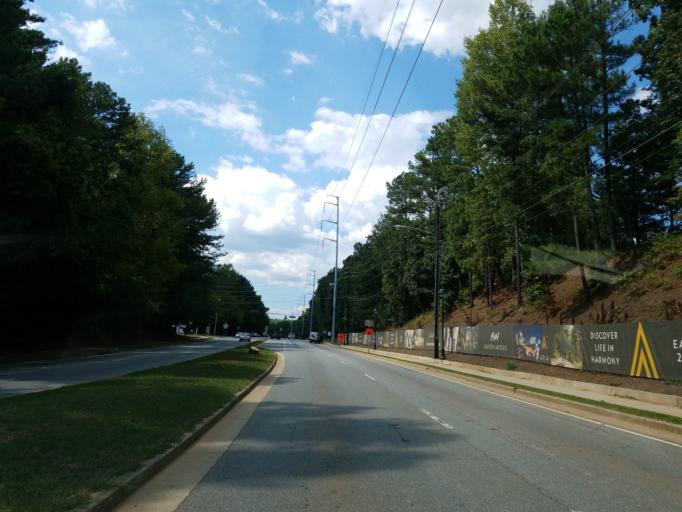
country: US
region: Georgia
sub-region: Fulton County
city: Sandy Springs
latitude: 33.9360
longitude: -84.3655
